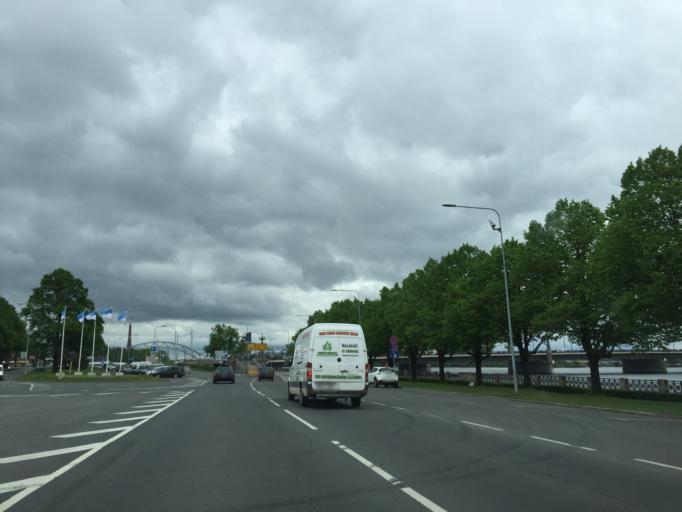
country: LV
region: Riga
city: Riga
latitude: 56.9480
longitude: 24.1024
